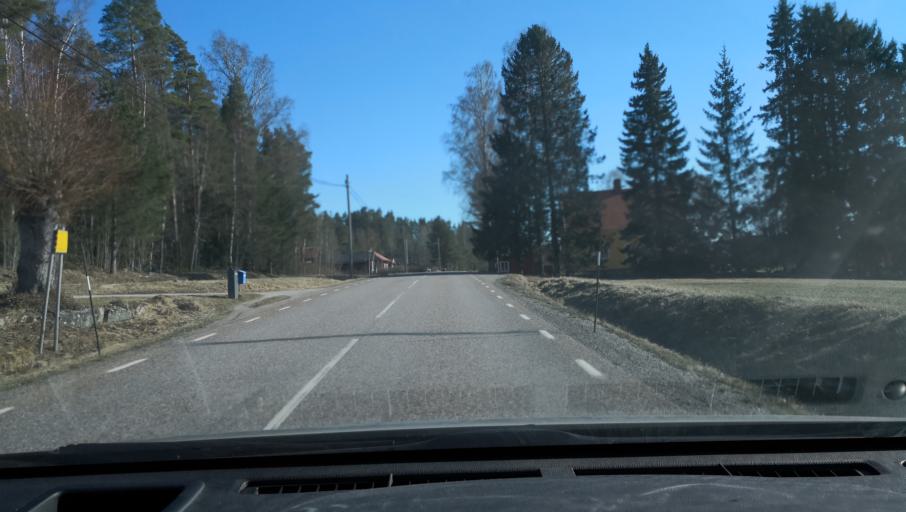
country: SE
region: Vaestmanland
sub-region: Surahammars Kommun
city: Ramnas
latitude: 59.9381
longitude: 16.3399
